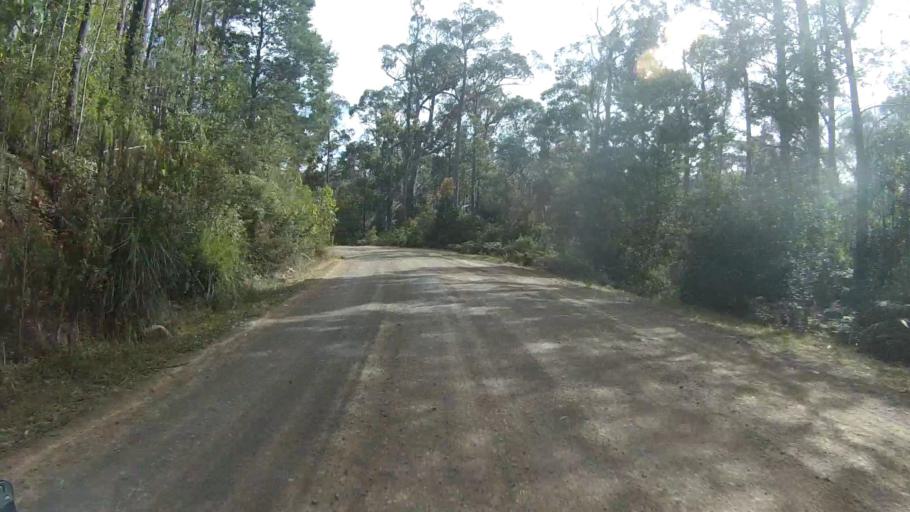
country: AU
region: Tasmania
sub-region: Sorell
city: Sorell
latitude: -42.7377
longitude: 147.8341
